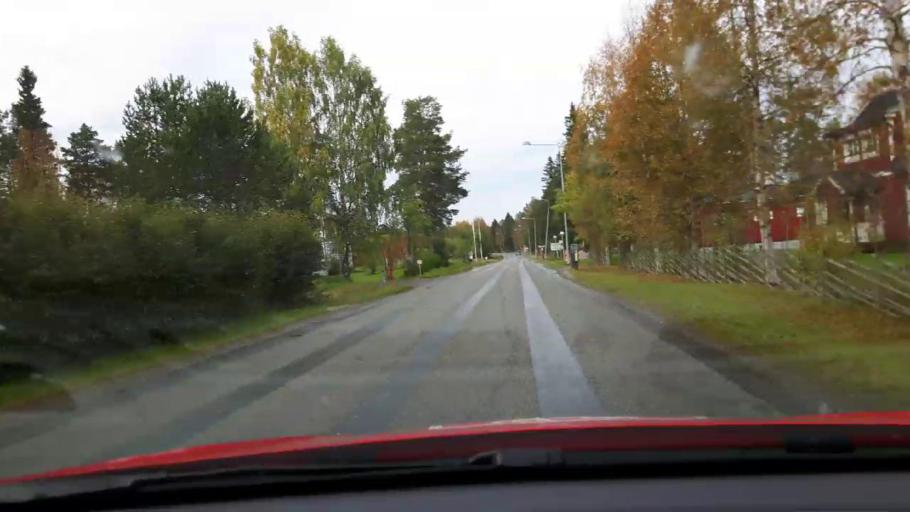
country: SE
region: Jaemtland
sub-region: Bergs Kommun
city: Hoverberg
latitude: 62.7702
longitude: 14.4289
